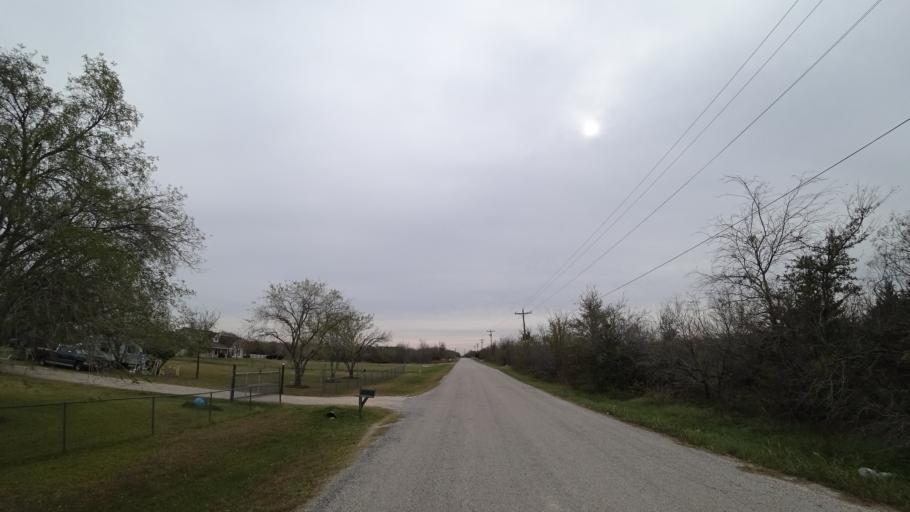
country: US
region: Texas
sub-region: Travis County
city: Garfield
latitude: 30.1107
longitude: -97.5788
